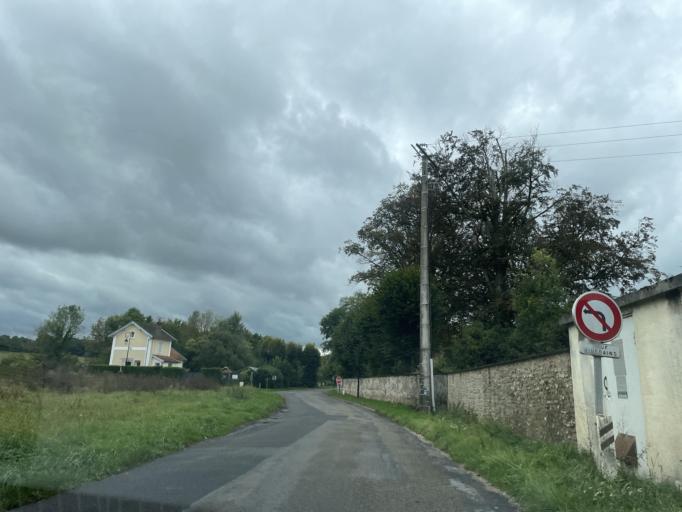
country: FR
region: Ile-de-France
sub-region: Departement de Seine-et-Marne
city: Boissy-le-Chatel
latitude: 48.8098
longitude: 3.1240
